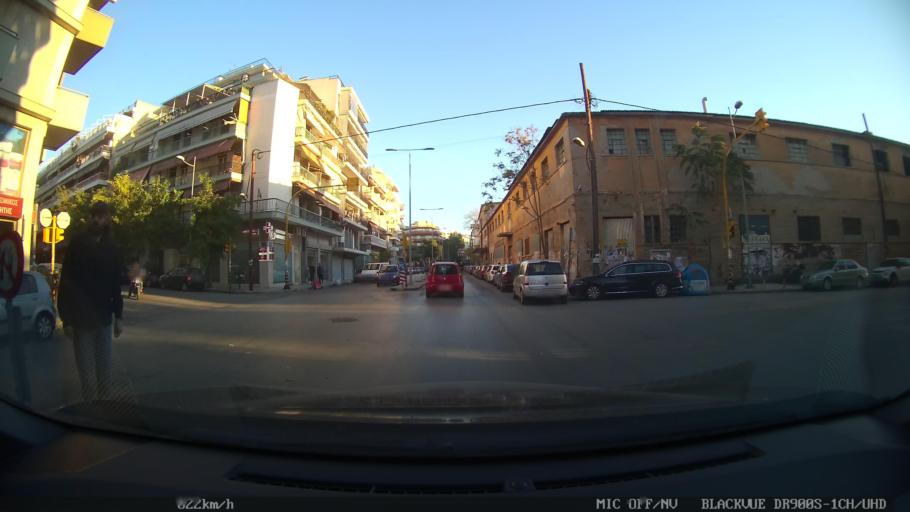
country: GR
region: Central Macedonia
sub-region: Nomos Thessalonikis
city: Triandria
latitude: 40.6064
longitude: 22.9675
